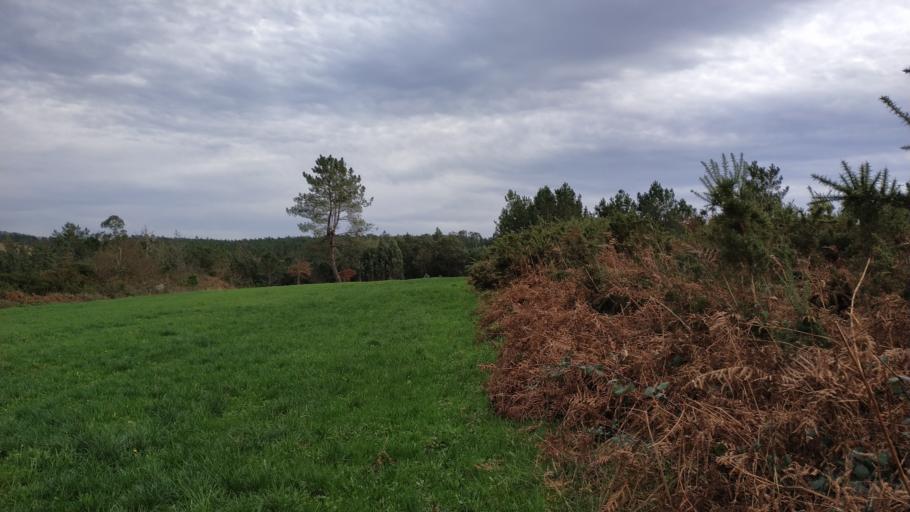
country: ES
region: Galicia
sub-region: Provincia de Pontevedra
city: Silleda
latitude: 42.7739
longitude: -8.1639
